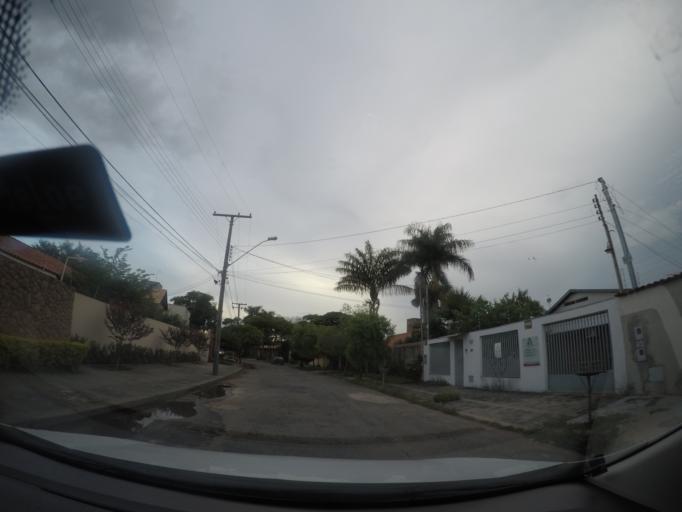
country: BR
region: Goias
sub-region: Goiania
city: Goiania
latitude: -16.6517
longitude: -49.2335
